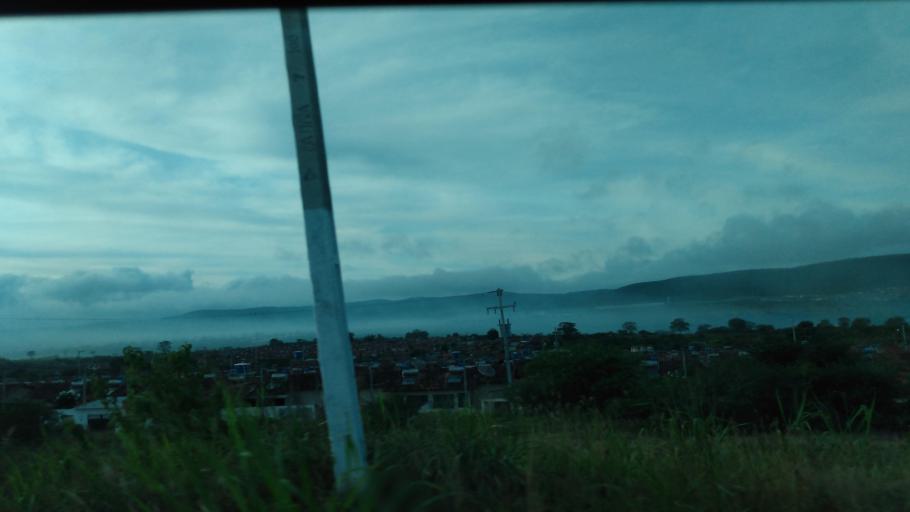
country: BR
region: Pernambuco
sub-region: Bezerros
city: Bezerros
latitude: -8.2143
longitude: -35.7427
